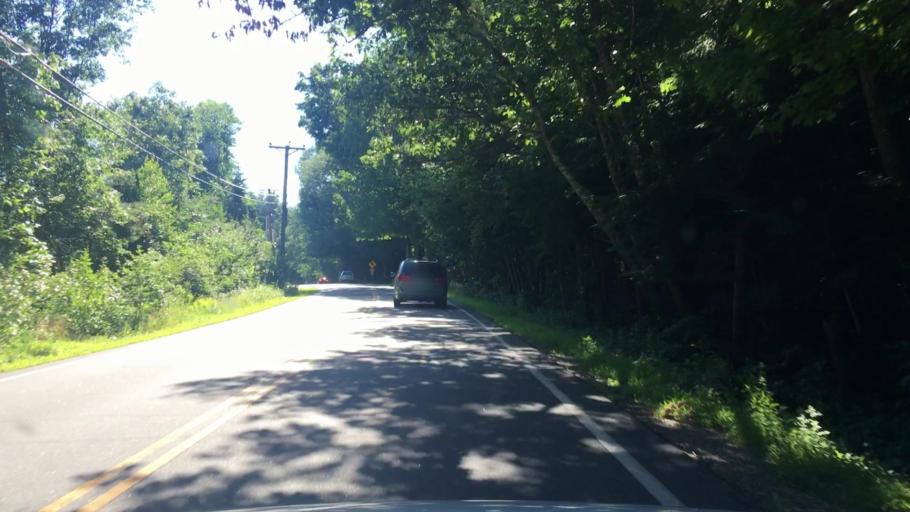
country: US
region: New Hampshire
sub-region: Rockingham County
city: Brentwood
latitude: 42.9914
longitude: -71.0356
